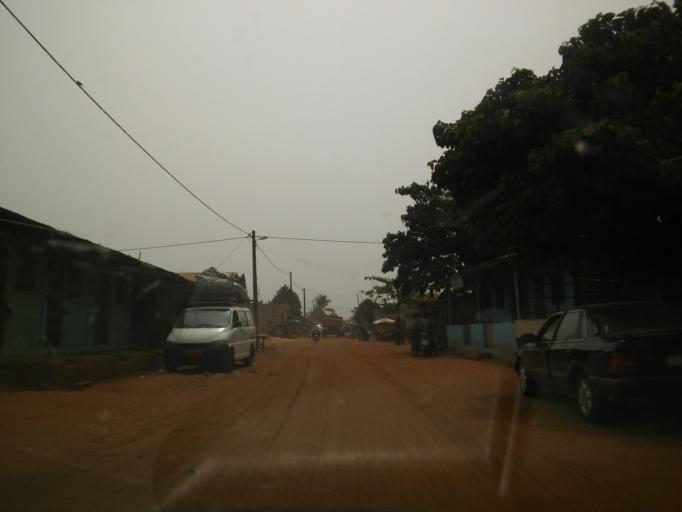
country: BJ
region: Mono
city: Come
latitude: 6.4063
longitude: 1.8817
